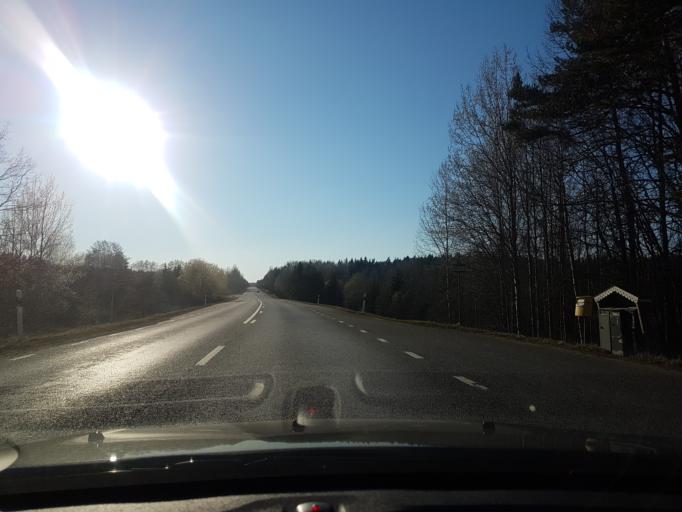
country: SE
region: Uppsala
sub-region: Heby Kommun
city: Morgongava
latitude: 59.8932
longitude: 17.1520
